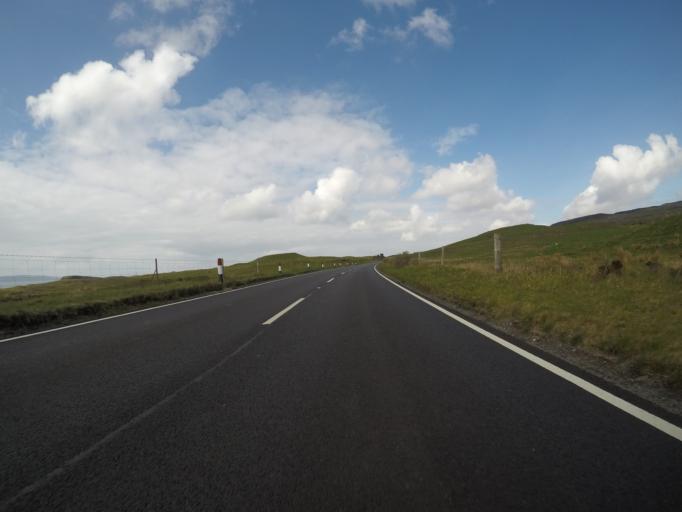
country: GB
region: Scotland
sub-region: Highland
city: Portree
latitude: 57.5423
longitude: -6.3647
